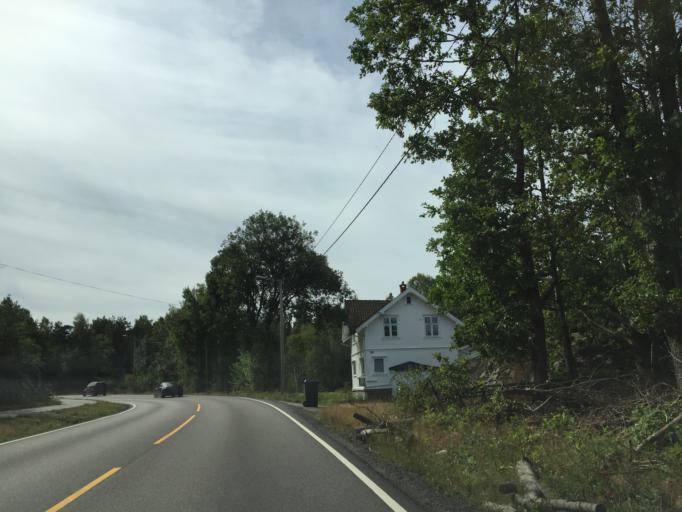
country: NO
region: Ostfold
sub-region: Fredrikstad
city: Fredrikstad
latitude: 59.1588
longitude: 10.9312
